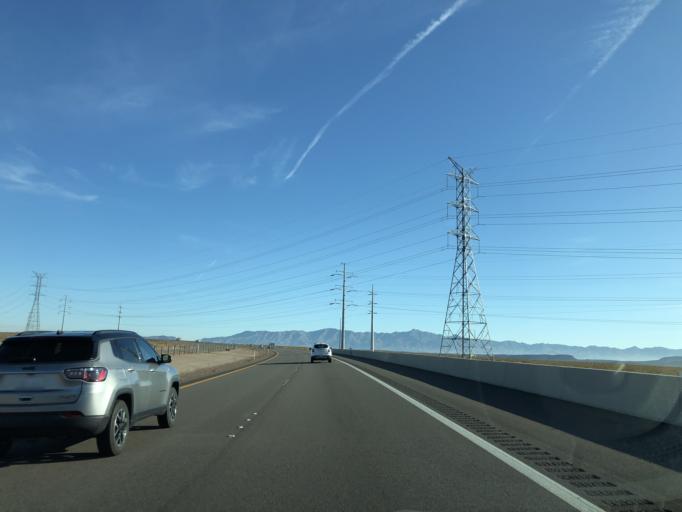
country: US
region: Nevada
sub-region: Clark County
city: Boulder City
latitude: 35.9408
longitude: -114.8157
